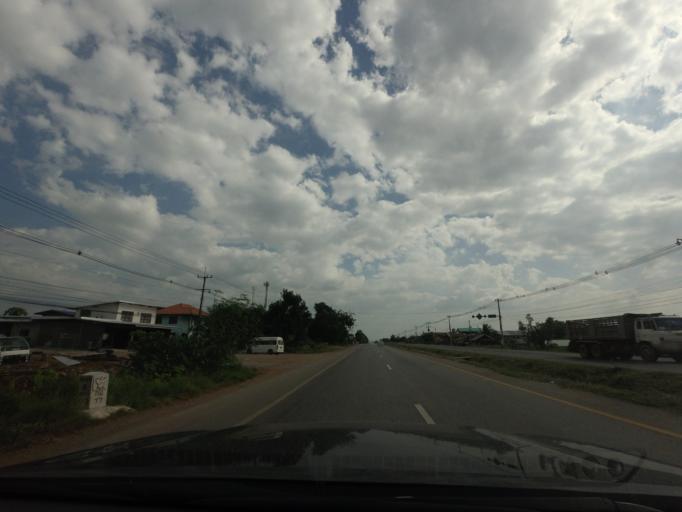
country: TH
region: Lop Buri
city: Chai Badan
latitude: 15.2527
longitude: 101.1255
